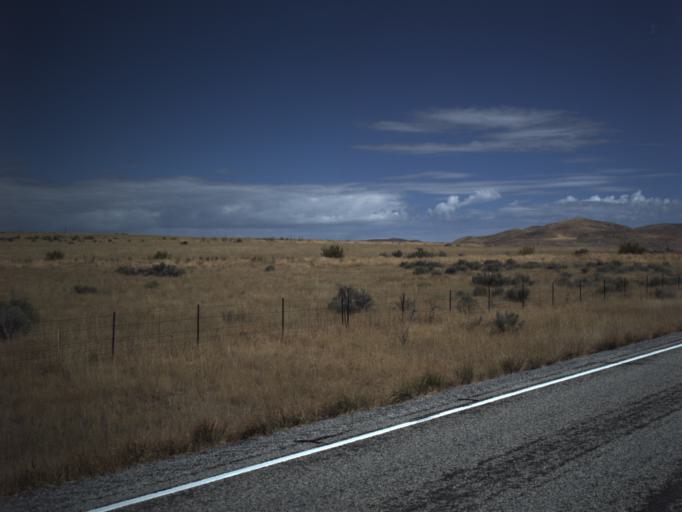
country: US
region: Utah
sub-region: Box Elder County
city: Garland
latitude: 41.7899
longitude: -112.4245
